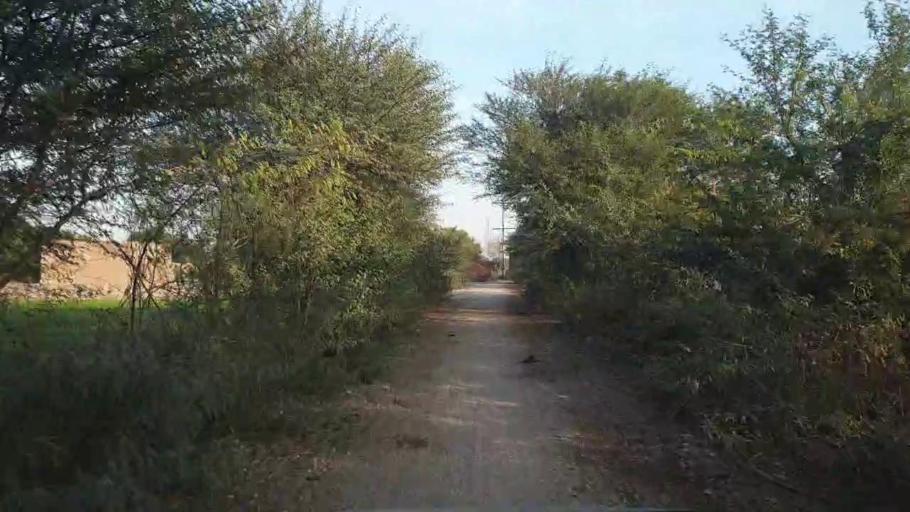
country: PK
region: Sindh
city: Chambar
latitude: 25.2763
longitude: 68.8078
